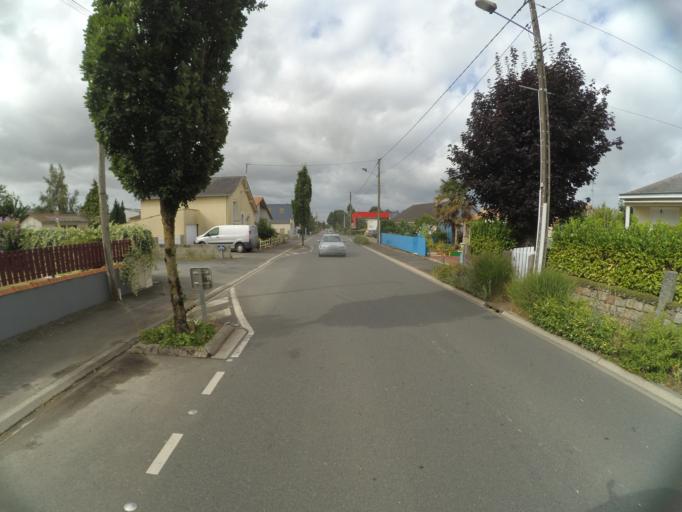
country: FR
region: Pays de la Loire
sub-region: Departement de Maine-et-Loire
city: Villedieu-la-Blouere
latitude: 47.1440
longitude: -1.0675
